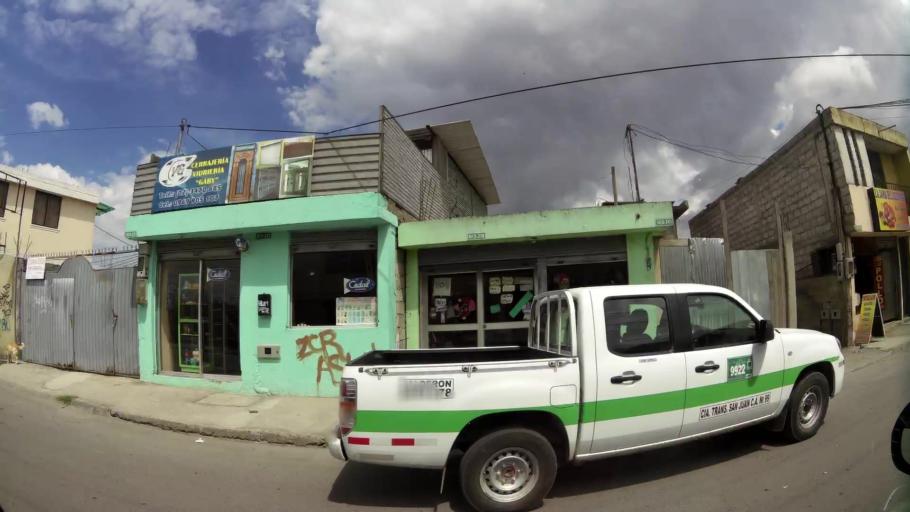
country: EC
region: Pichincha
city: Quito
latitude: -0.0638
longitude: -78.4316
